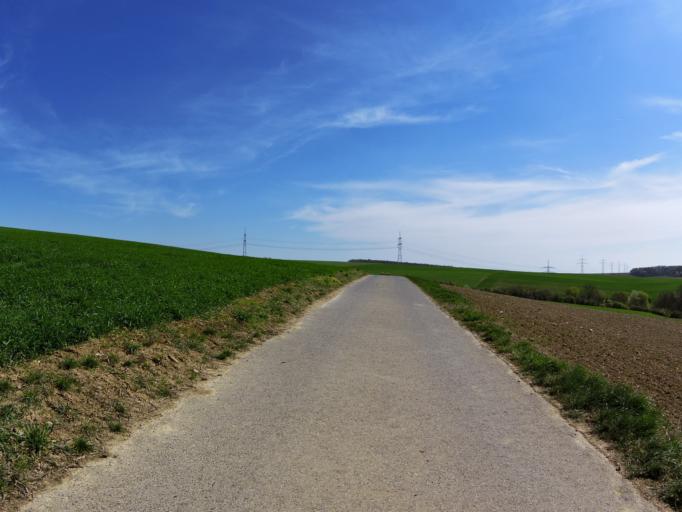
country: DE
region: Bavaria
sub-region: Regierungsbezirk Unterfranken
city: Rottendorf
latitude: 49.7924
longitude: 10.0422
